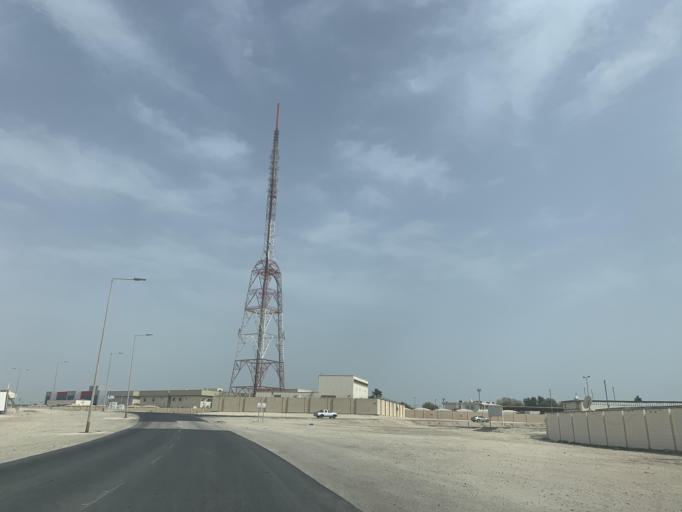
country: BH
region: Northern
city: Madinat `Isa
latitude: 26.1606
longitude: 50.5547
